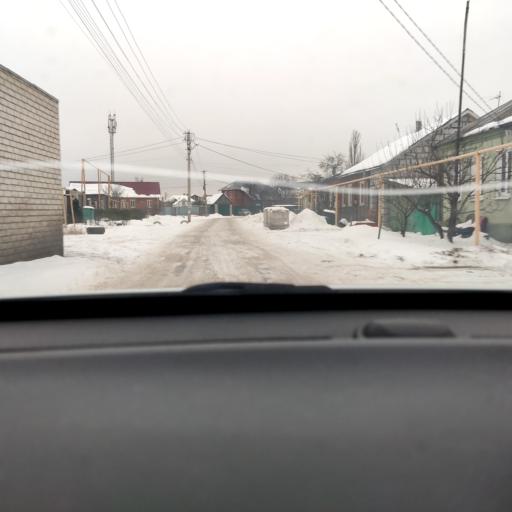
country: RU
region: Voronezj
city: Somovo
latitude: 51.7490
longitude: 39.3403
